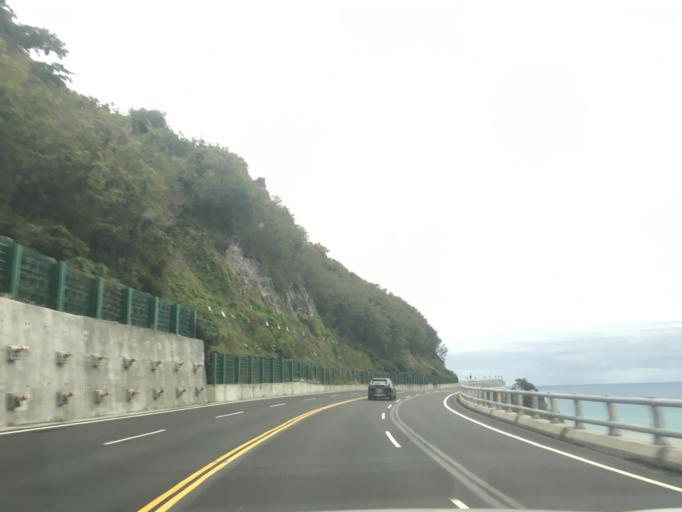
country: TW
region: Taiwan
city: Hengchun
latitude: 22.3923
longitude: 120.9169
